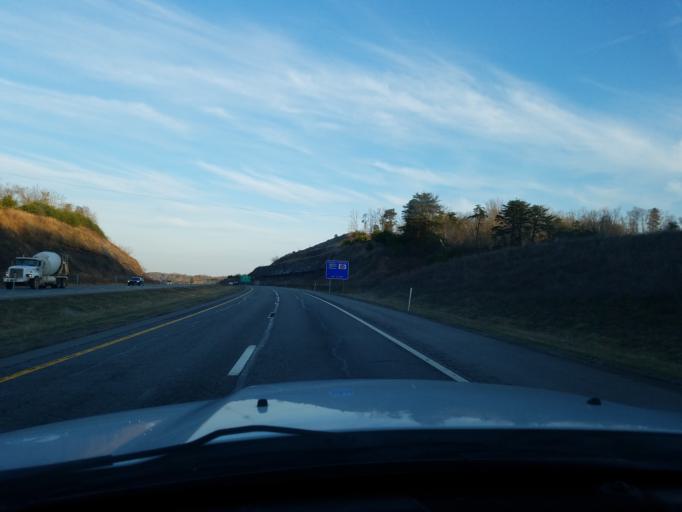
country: US
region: West Virginia
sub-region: Putnam County
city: Teays Valley
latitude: 38.4711
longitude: -81.9117
